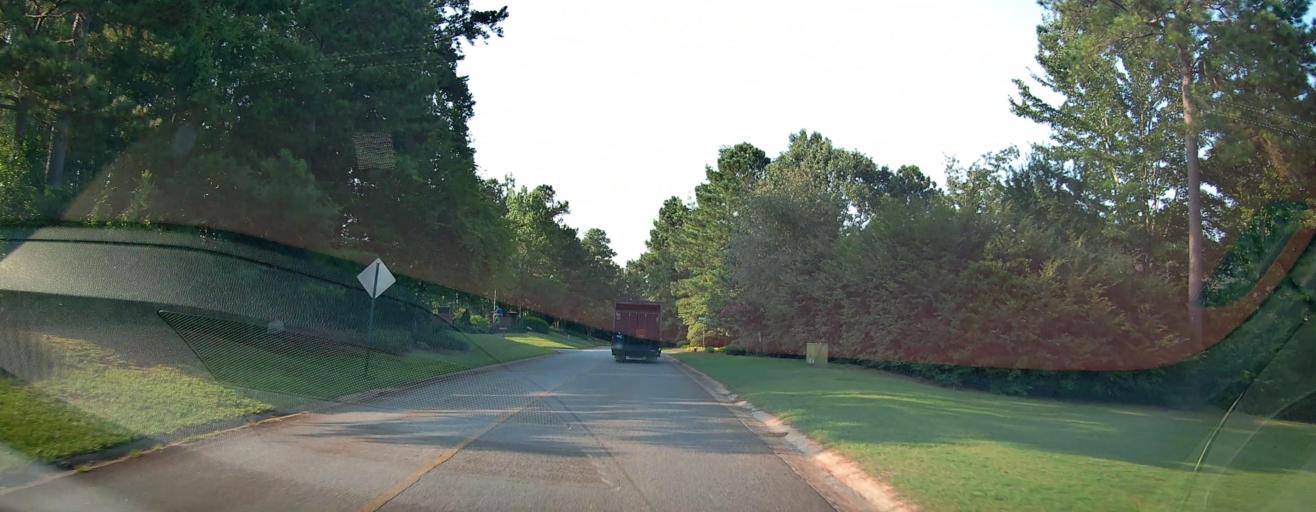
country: US
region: Georgia
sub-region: Bibb County
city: West Point
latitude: 32.8853
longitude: -83.8146
